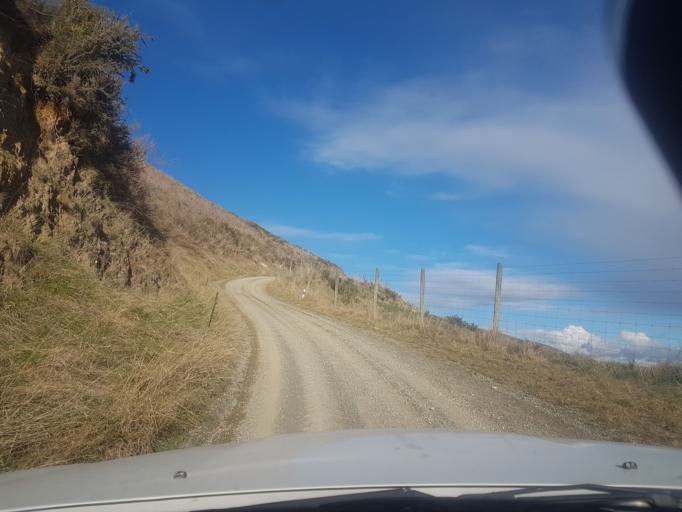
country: NZ
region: Canterbury
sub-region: Timaru District
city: Pleasant Point
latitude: -44.1692
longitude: 170.8823
